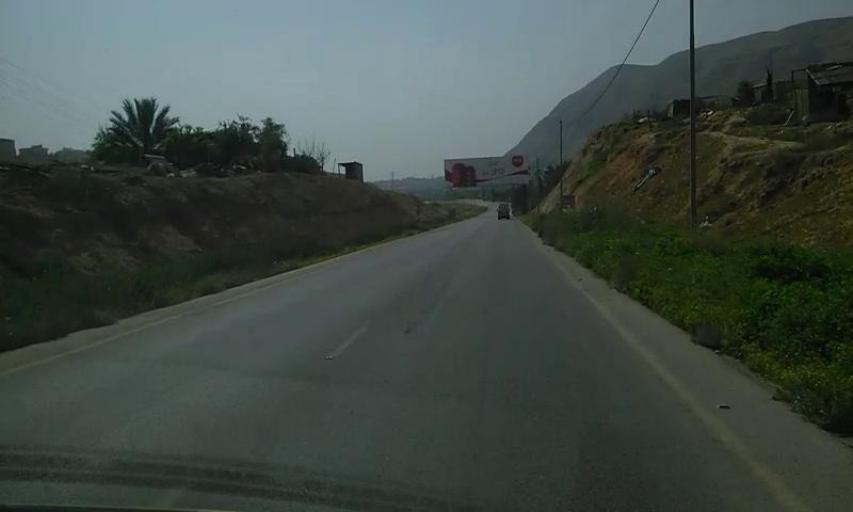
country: PS
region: West Bank
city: An Nuway`imah
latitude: 31.8951
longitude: 35.4286
